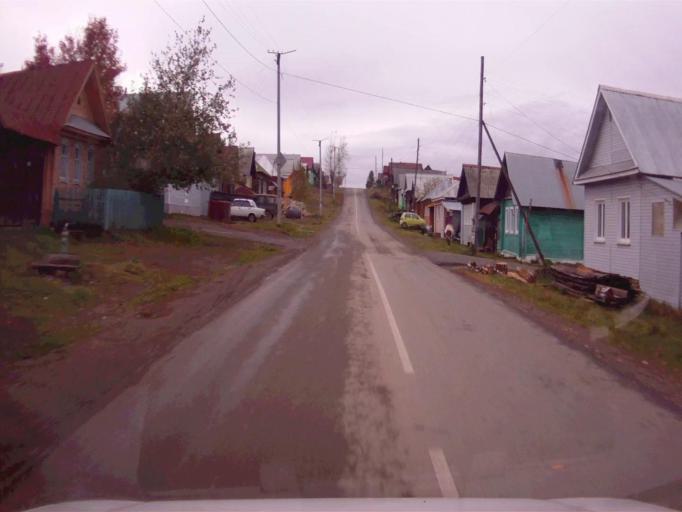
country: RU
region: Chelyabinsk
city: Nyazepetrovsk
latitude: 56.0613
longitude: 59.5774
